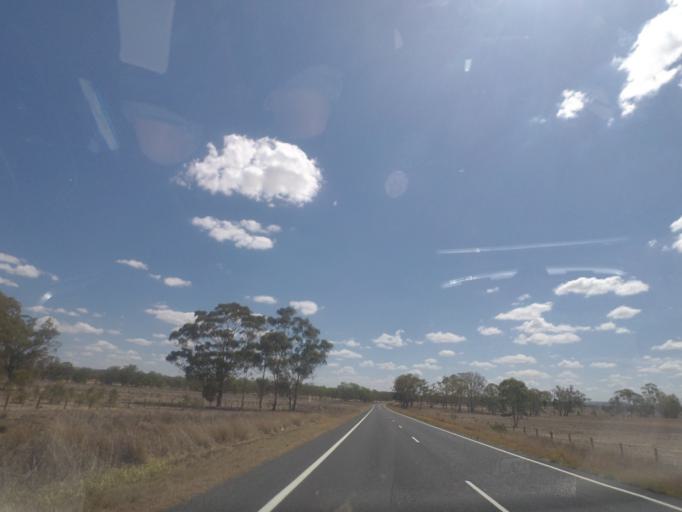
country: AU
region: Queensland
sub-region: Southern Downs
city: Warwick
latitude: -28.1815
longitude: 151.8201
